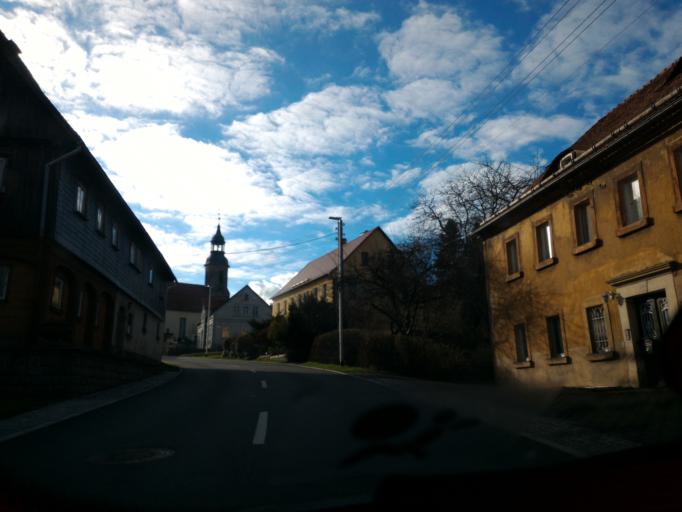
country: DE
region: Saxony
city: Grossschonau
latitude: 50.8707
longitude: 14.6516
